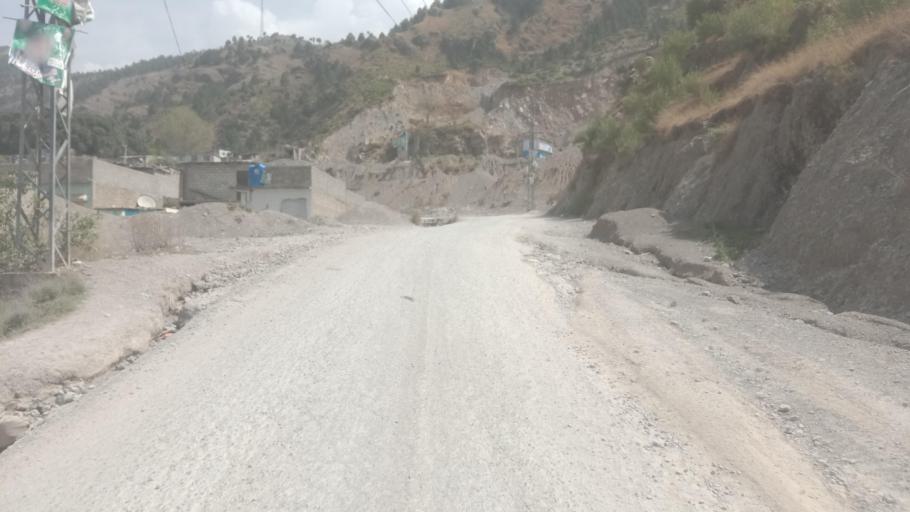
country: PK
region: Khyber Pakhtunkhwa
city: Abbottabad
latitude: 34.1620
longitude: 73.2797
